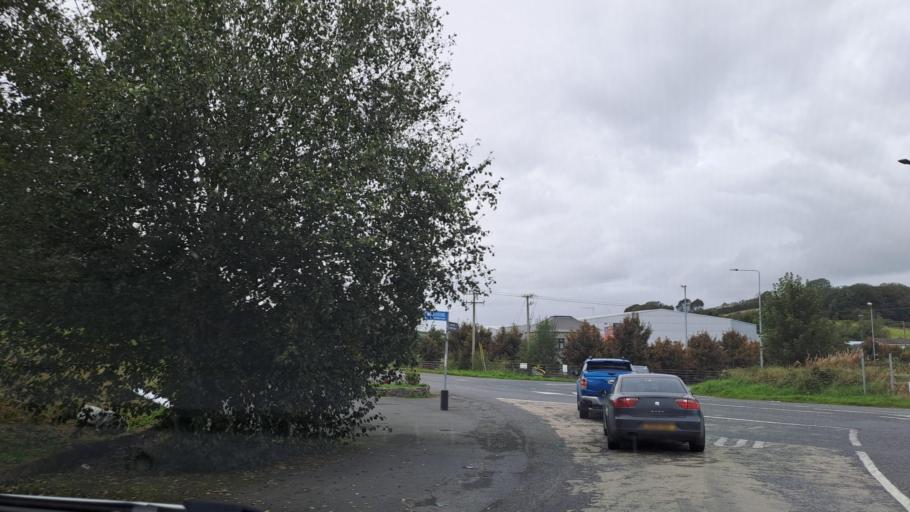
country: IE
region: Ulster
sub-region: County Monaghan
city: Castleblayney
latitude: 54.0650
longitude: -6.8126
